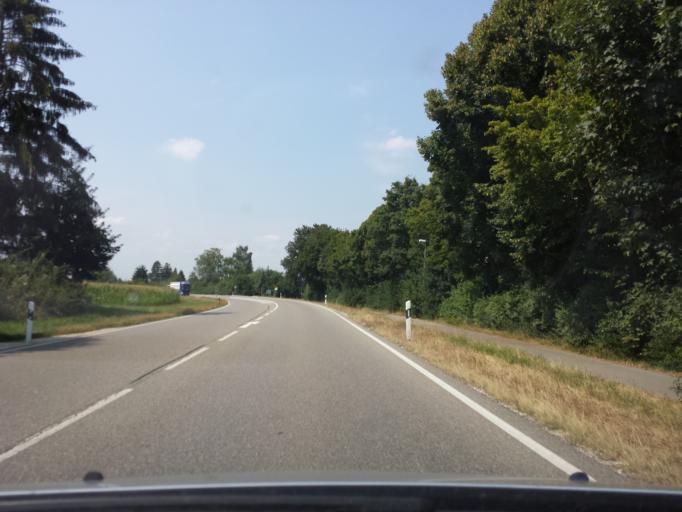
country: DE
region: Bavaria
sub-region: Swabia
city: Nersingen
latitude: 48.4293
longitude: 10.1547
